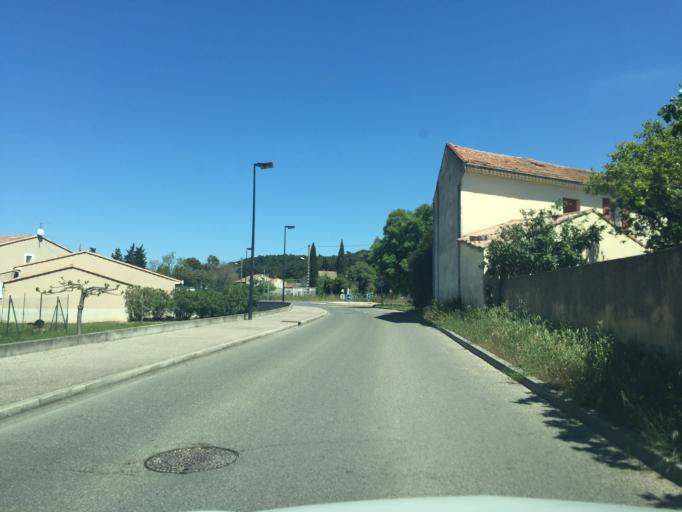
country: FR
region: Provence-Alpes-Cote d'Azur
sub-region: Departement du Vaucluse
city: Orange
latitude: 44.1193
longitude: 4.8006
